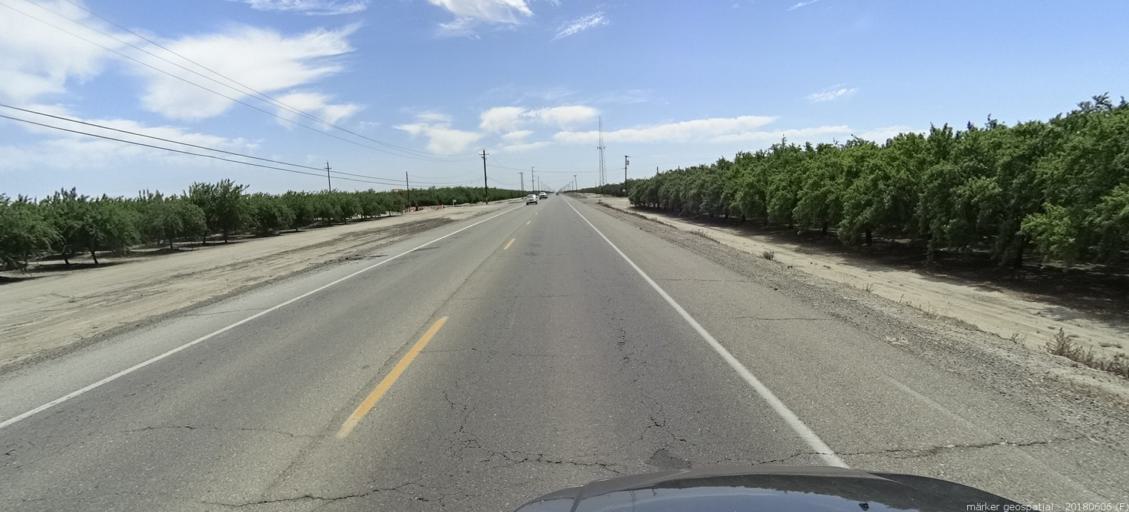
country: US
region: California
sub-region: Fresno County
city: Firebaugh
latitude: 36.8585
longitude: -120.4012
